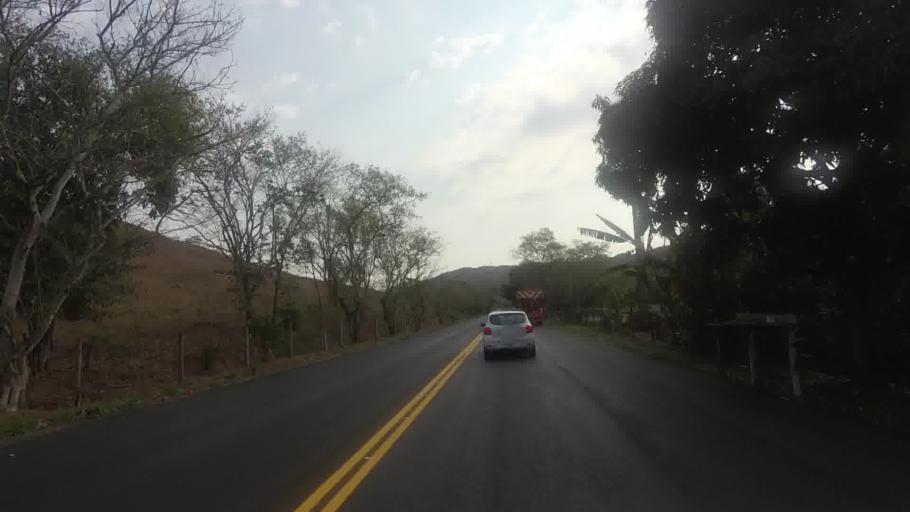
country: BR
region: Rio de Janeiro
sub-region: Bom Jesus Do Itabapoana
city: Bom Jesus do Itabapoana
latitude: -21.2114
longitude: -41.7290
